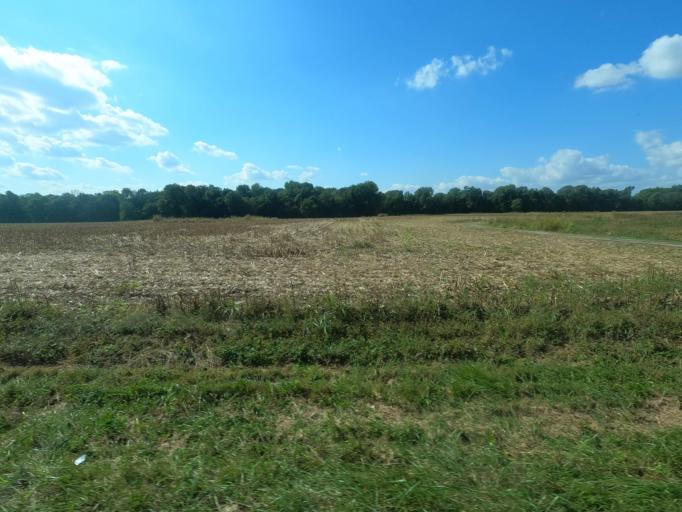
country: US
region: Illinois
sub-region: Massac County
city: Metropolis
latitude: 37.2056
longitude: -88.7292
